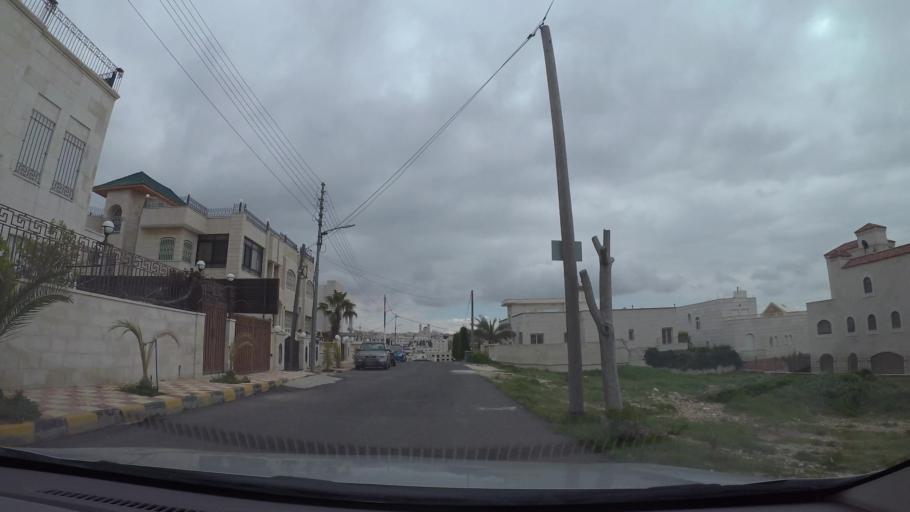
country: JO
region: Amman
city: Wadi as Sir
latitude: 31.9913
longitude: 35.8352
